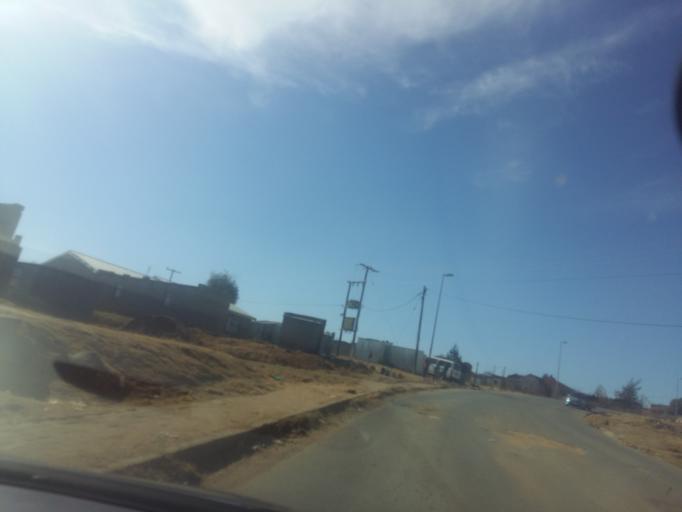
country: LS
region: Maseru
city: Maseru
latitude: -29.3933
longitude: 27.5205
